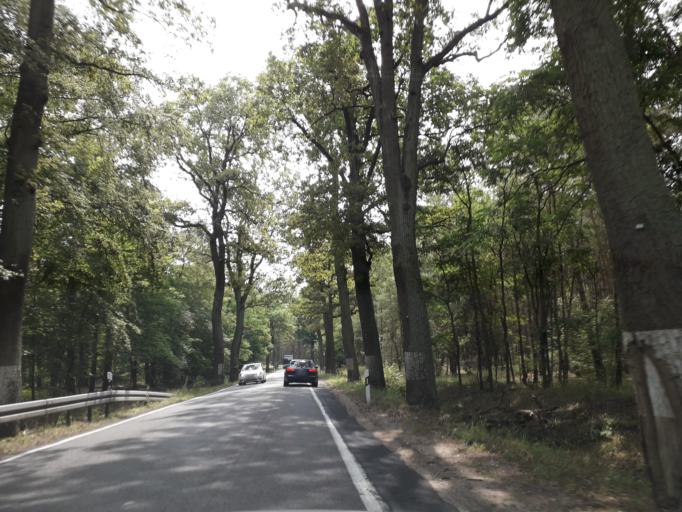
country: DE
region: Brandenburg
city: Falkensee
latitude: 52.6156
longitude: 13.1048
